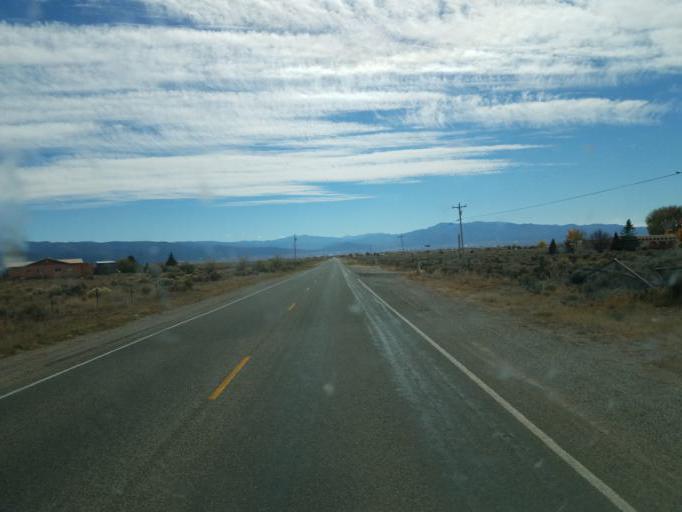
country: US
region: New Mexico
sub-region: Taos County
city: Arroyo Seco
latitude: 36.4874
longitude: -105.5938
